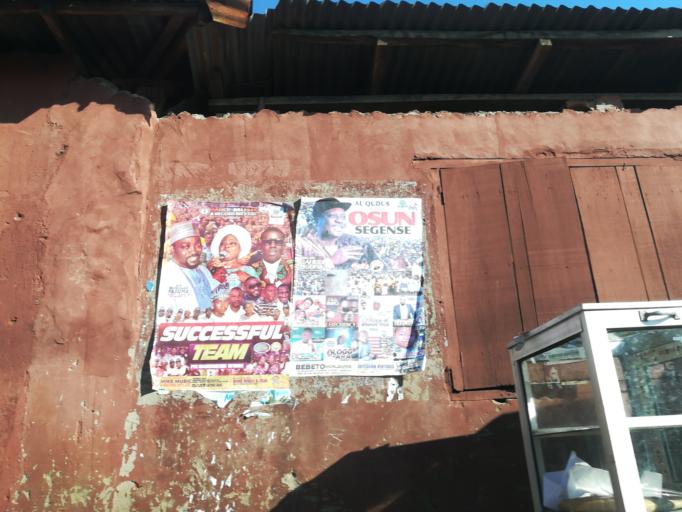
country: NG
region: Lagos
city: Ikorodu
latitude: 6.5377
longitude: 3.5522
